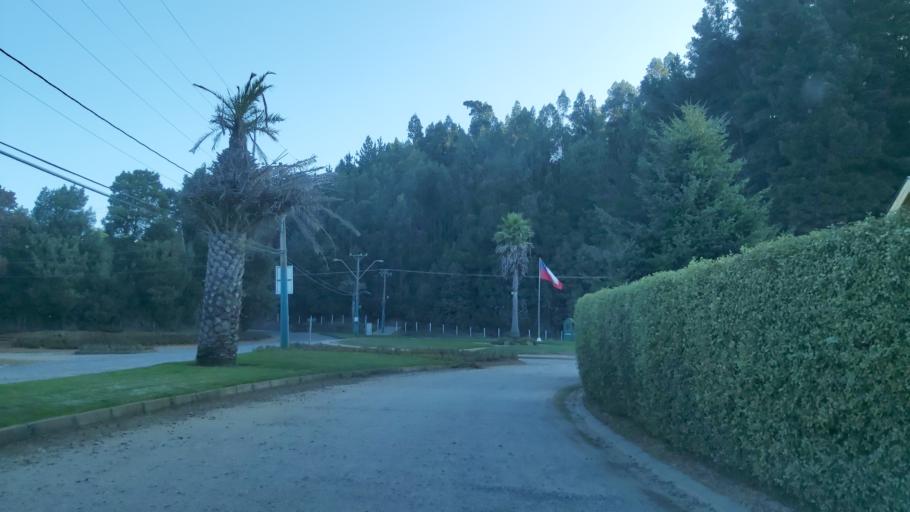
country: CL
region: Biobio
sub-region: Provincia de Concepcion
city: Tome
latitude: -36.5337
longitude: -72.9304
